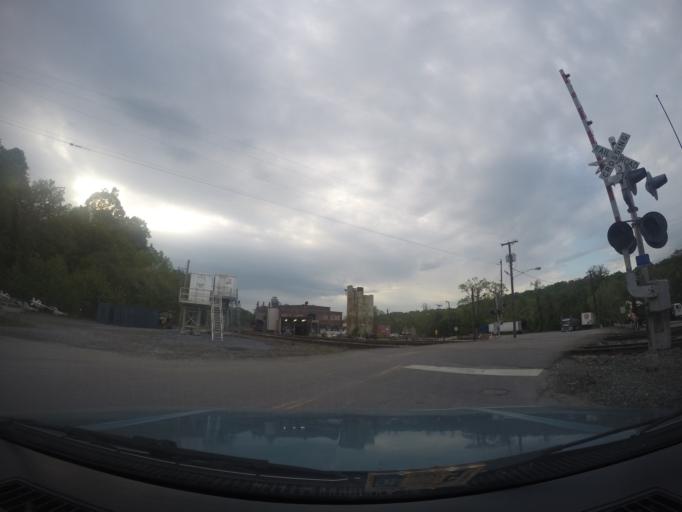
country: US
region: Virginia
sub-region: City of Lynchburg
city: Lynchburg
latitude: 37.3986
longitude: -79.1230
